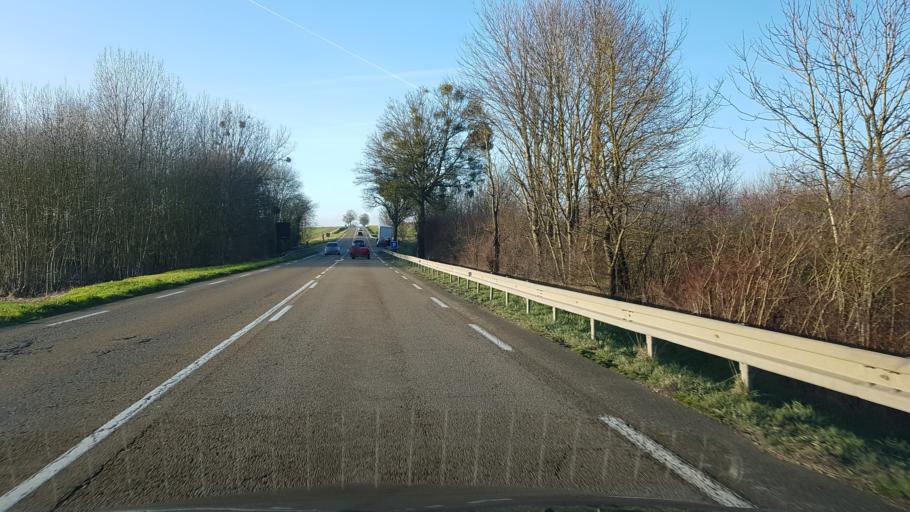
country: FR
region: Champagne-Ardenne
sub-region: Departement de la Marne
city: Vitry-le-Francois
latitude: 48.7372
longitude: 4.5469
